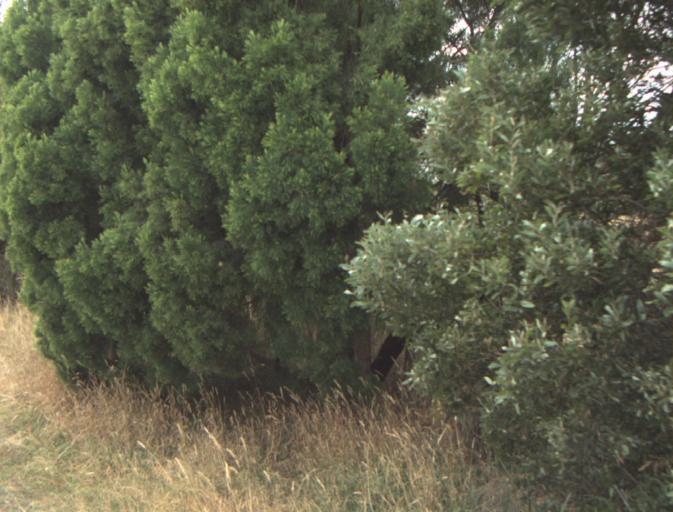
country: AU
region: Tasmania
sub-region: Launceston
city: Mayfield
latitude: -41.2963
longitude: 146.9857
